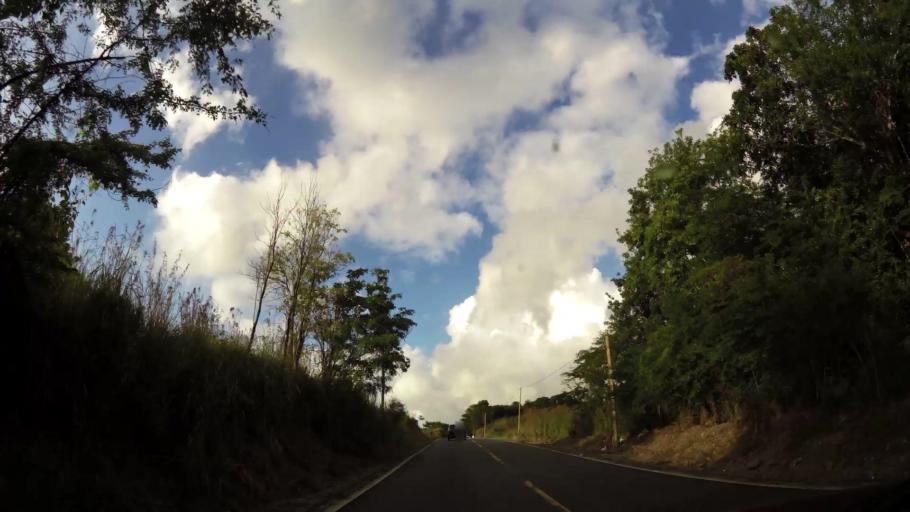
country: DM
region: Saint John
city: Portsmouth
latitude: 15.5360
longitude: -61.4746
